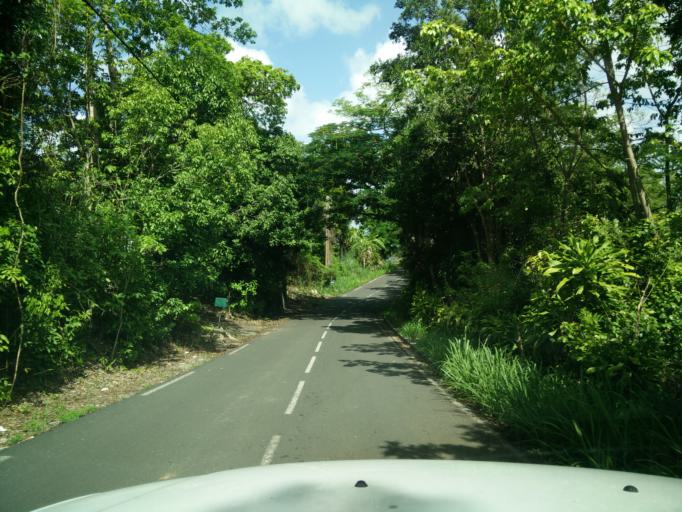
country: GP
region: Guadeloupe
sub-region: Guadeloupe
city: Le Gosier
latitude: 16.2293
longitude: -61.4692
